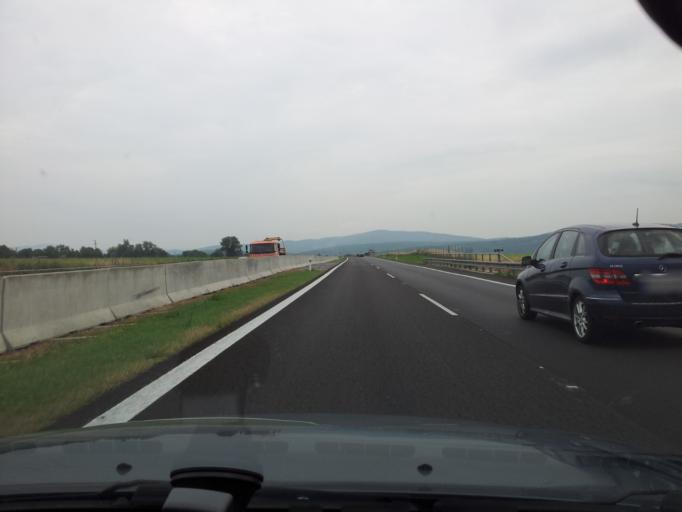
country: SK
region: Banskobystricky
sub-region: Okres Banska Bystrica
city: Zvolen
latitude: 48.6559
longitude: 19.1268
